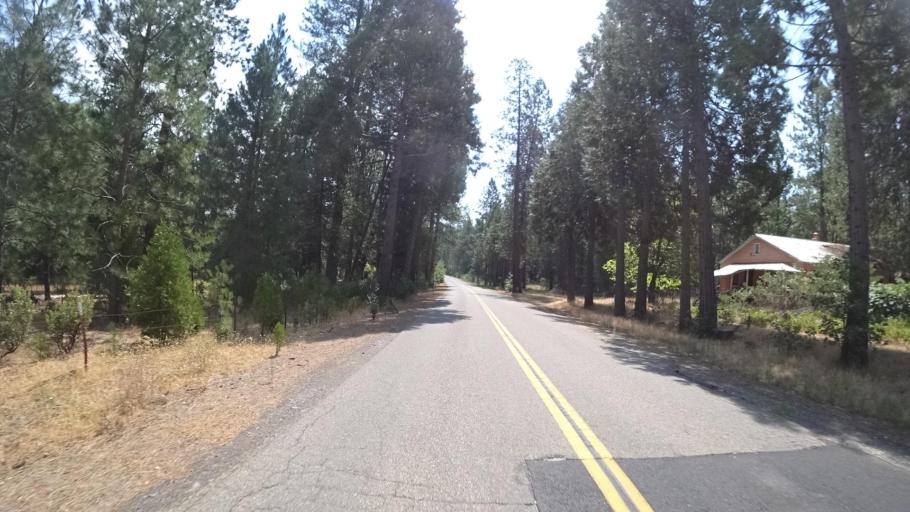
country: US
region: California
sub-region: Mariposa County
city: Midpines
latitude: 37.7232
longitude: -120.1025
